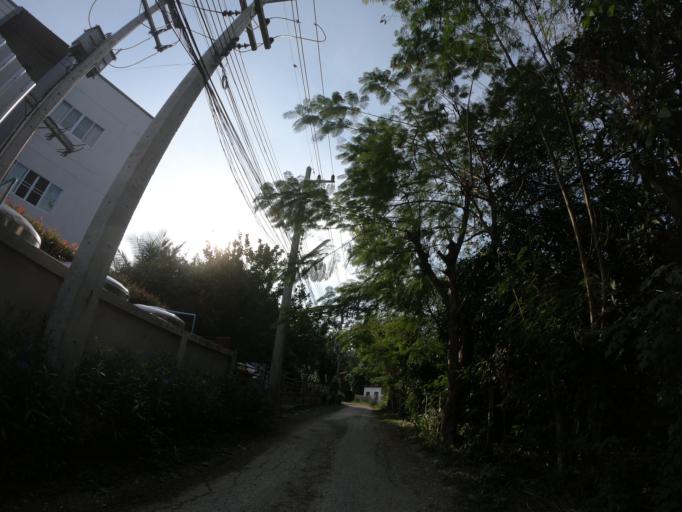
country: TH
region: Chiang Mai
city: Chiang Mai
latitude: 18.8204
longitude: 98.9905
